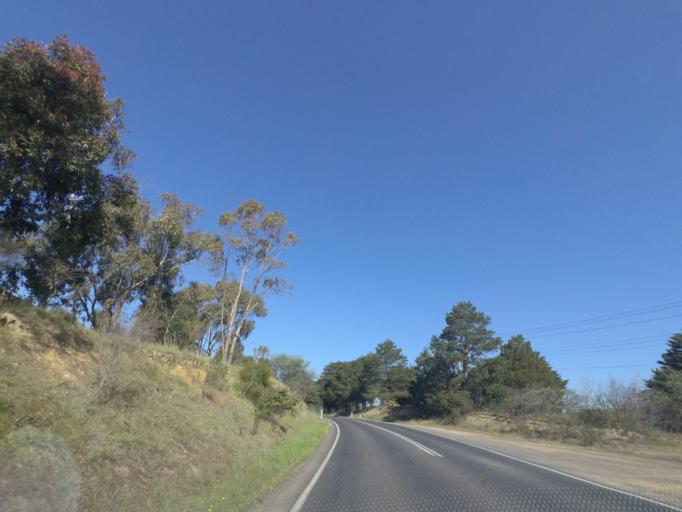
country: AU
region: Victoria
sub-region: Whittlesea
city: Whittlesea
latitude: -37.3466
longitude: 144.9997
